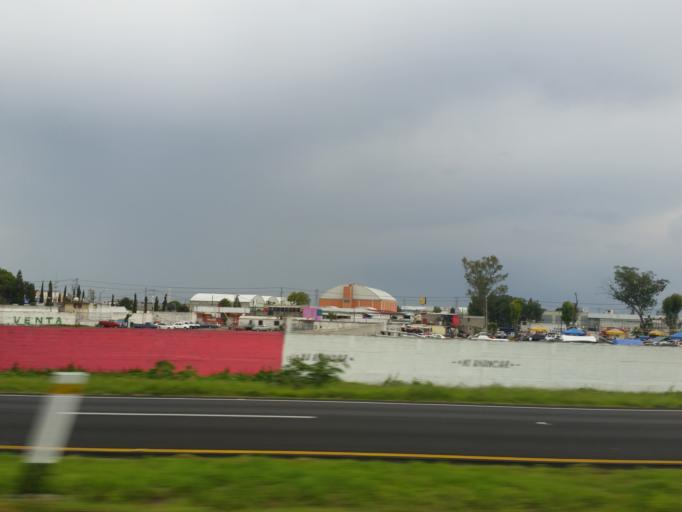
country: MX
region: Mexico
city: Santo Tomas Chiconautla
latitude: 19.6232
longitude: -98.9992
